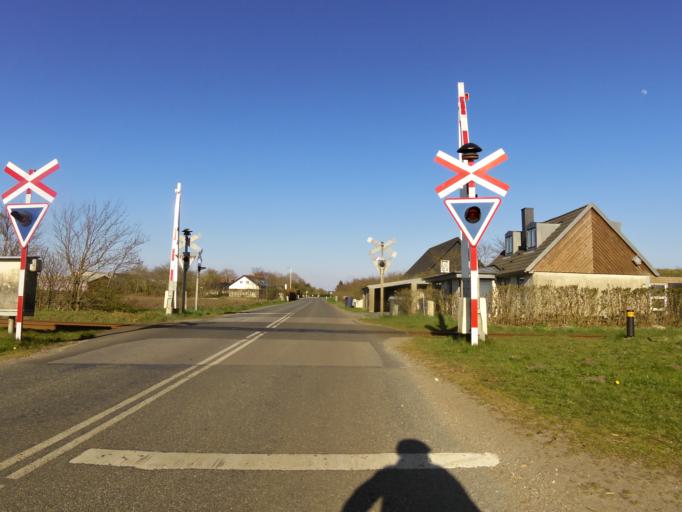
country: DK
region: South Denmark
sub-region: Esbjerg Kommune
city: Ribe
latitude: 55.3593
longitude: 8.7614
